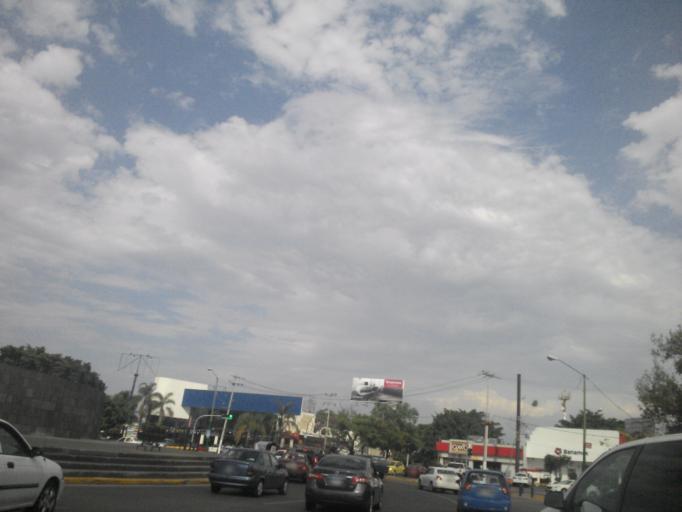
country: MX
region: Jalisco
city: Guadalajara
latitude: 20.6667
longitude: -103.3689
